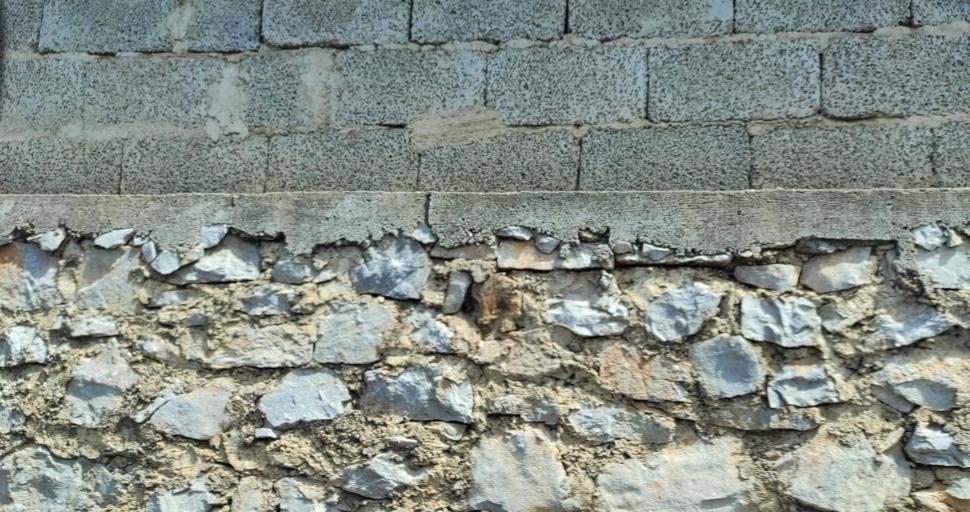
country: AL
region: Shkoder
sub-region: Rrethi i Malesia e Madhe
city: Gruemire
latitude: 42.1308
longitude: 19.5513
